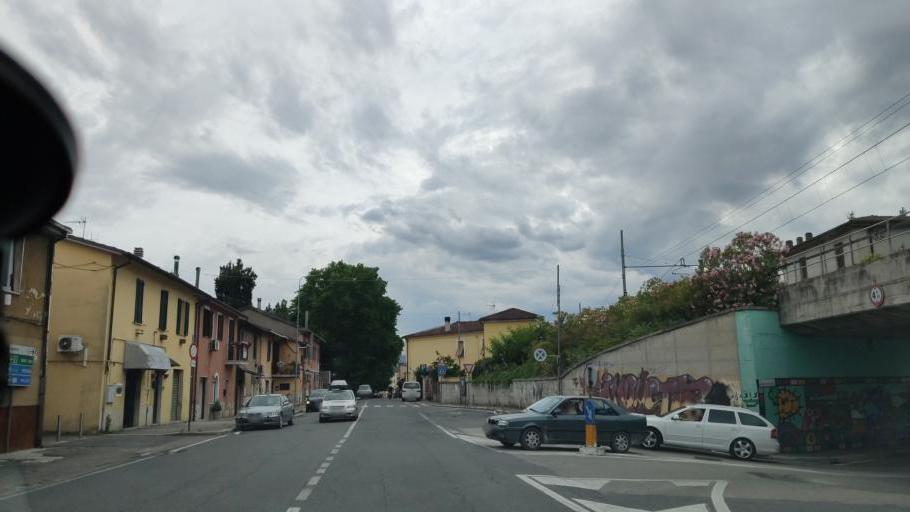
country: IT
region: Umbria
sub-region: Provincia di Terni
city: Terni
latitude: 42.5728
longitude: 12.6694
